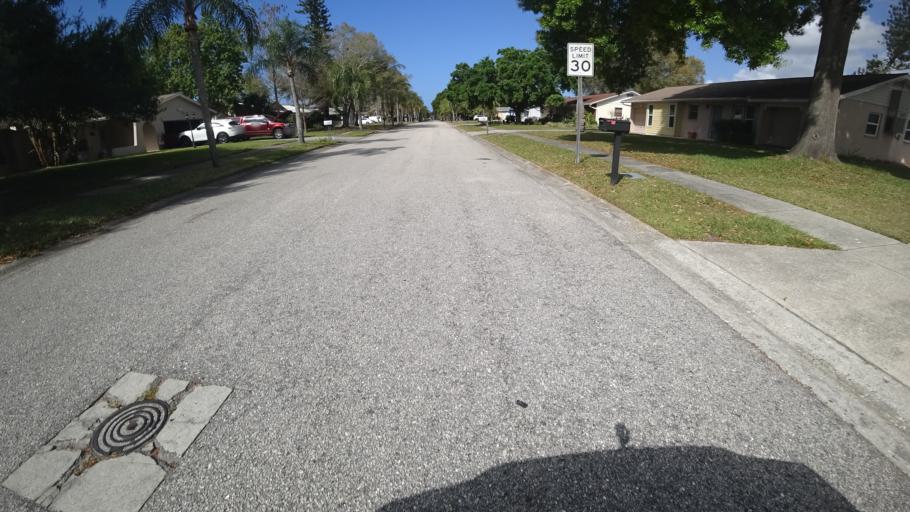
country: US
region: Florida
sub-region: Manatee County
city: Whitfield
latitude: 27.4107
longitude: -82.5553
